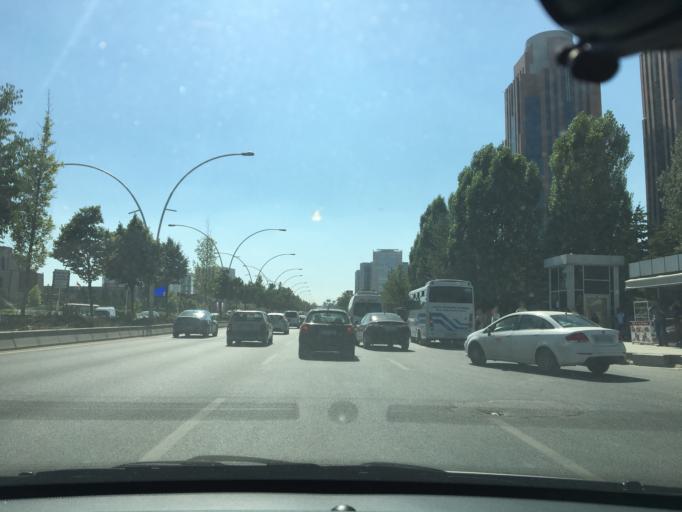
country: TR
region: Ankara
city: Batikent
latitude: 39.9079
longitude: 32.7638
